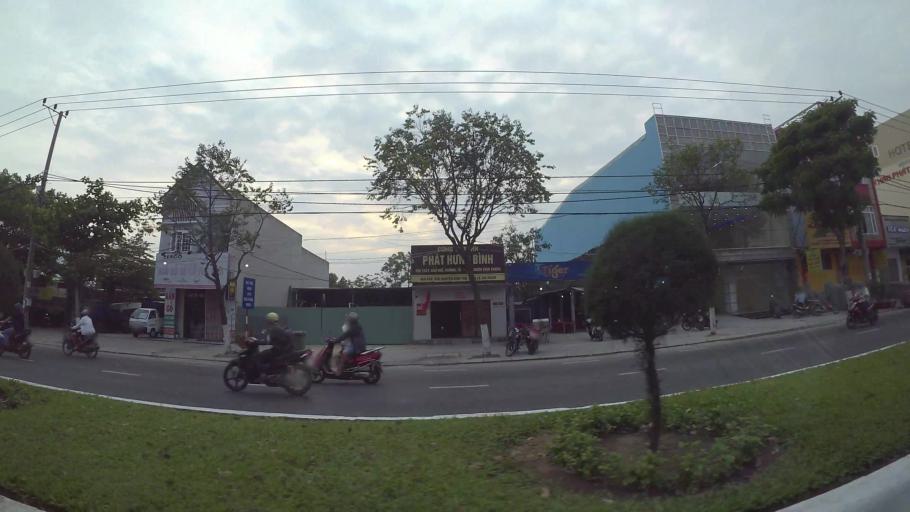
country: VN
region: Da Nang
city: Cam Le
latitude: 16.0267
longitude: 108.2088
